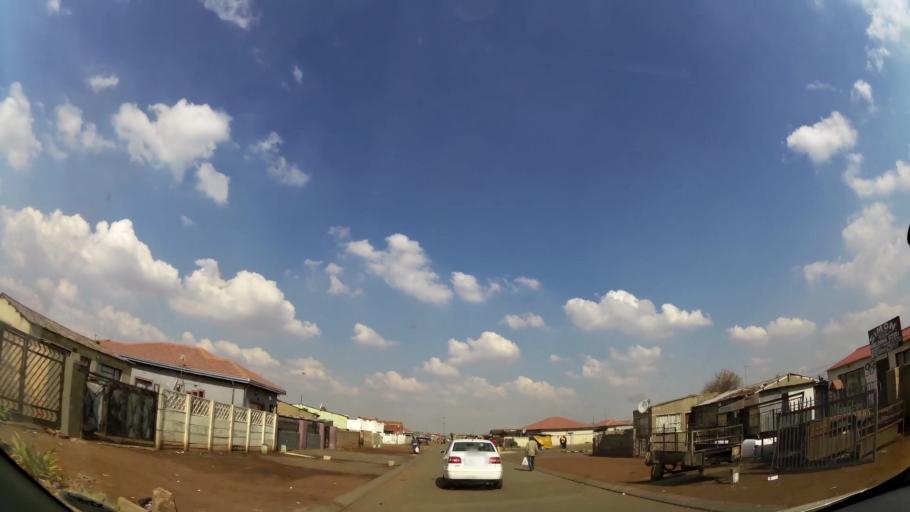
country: ZA
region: Gauteng
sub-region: Ekurhuleni Metropolitan Municipality
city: Germiston
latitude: -26.3371
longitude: 28.1446
